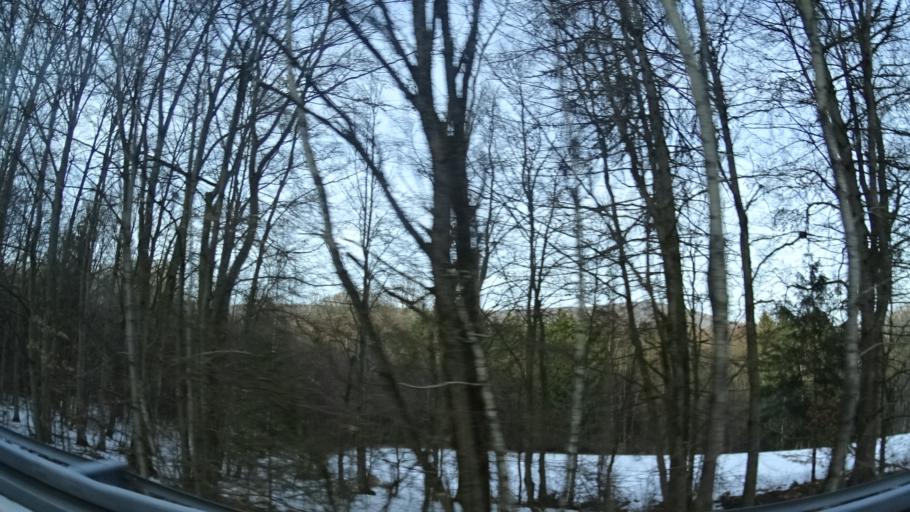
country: DE
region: Bavaria
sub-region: Regierungsbezirk Unterfranken
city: Sandberg
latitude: 50.3491
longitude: 9.9549
